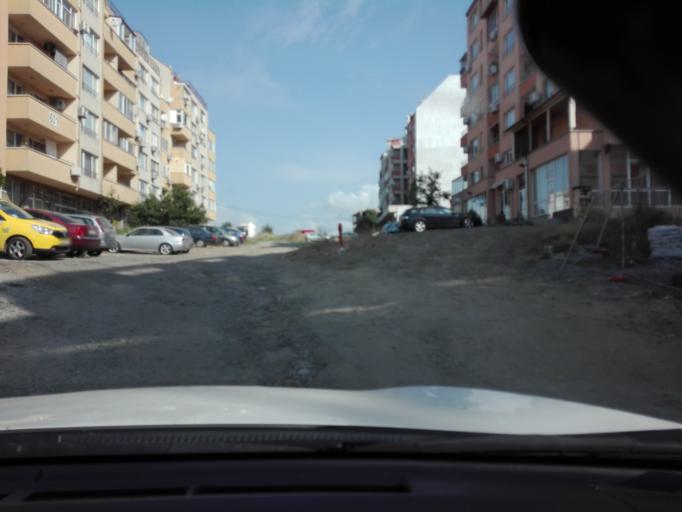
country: BG
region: Burgas
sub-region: Obshtina Burgas
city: Burgas
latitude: 42.4528
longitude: 27.4176
